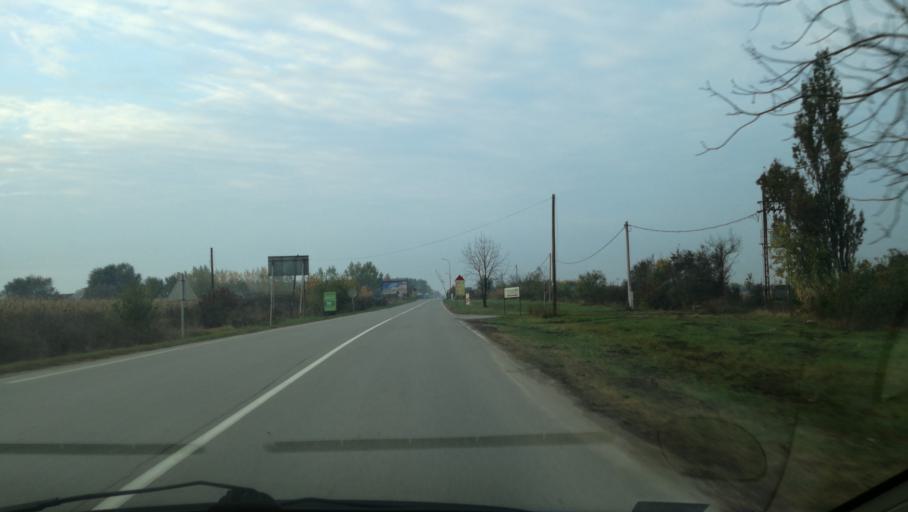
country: RS
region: Autonomna Pokrajina Vojvodina
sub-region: Severnobanatski Okrug
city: Kikinda
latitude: 45.7966
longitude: 20.4389
